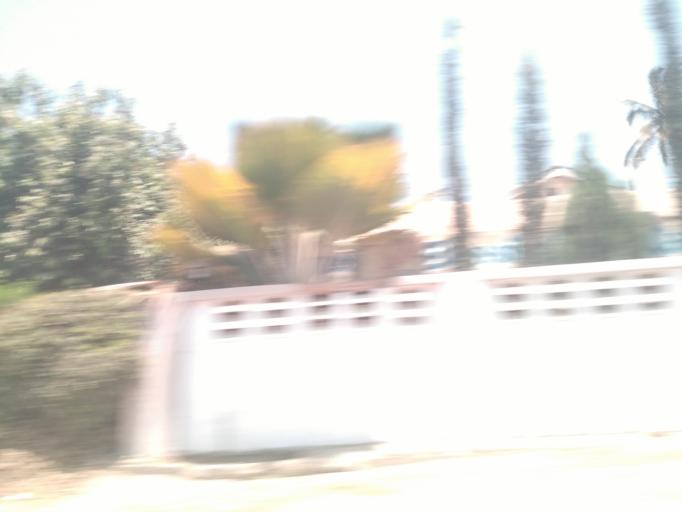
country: TZ
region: Dodoma
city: Dodoma
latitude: -6.1747
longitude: 35.7475
